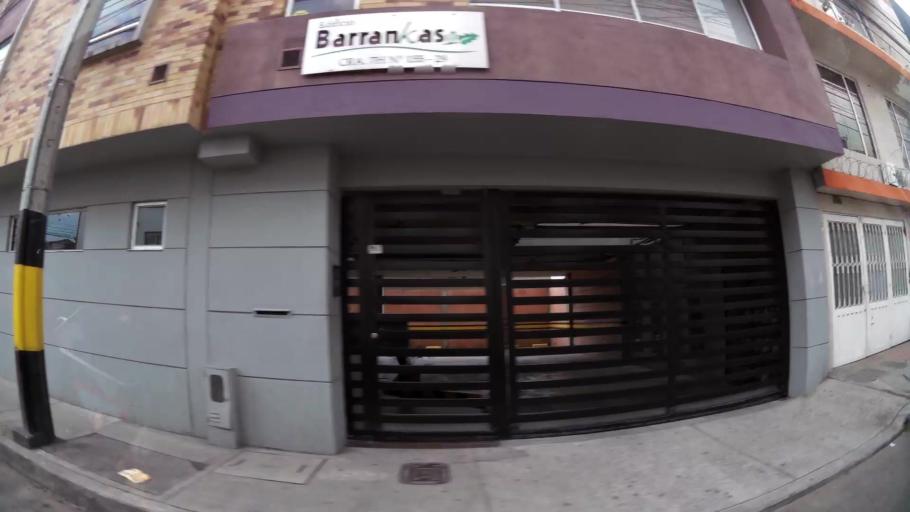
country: CO
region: Cundinamarca
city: La Calera
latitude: 4.7316
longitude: -74.0283
